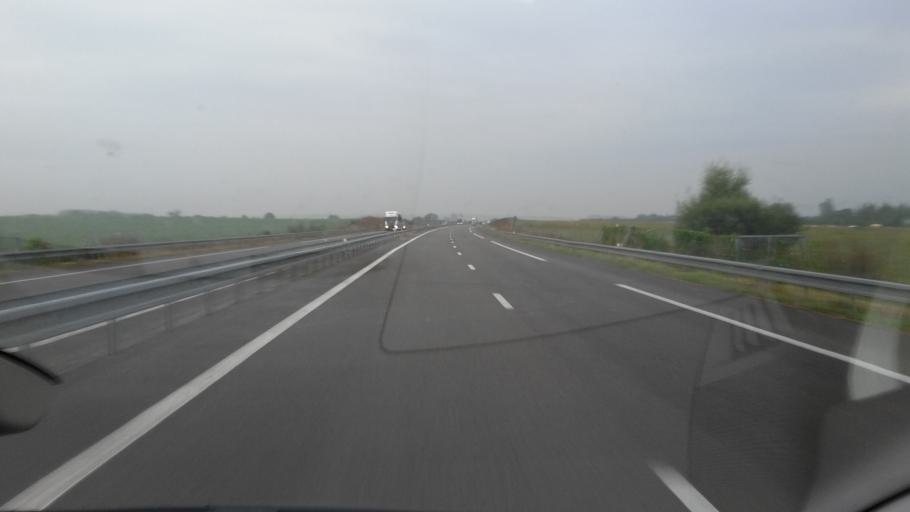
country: FR
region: Champagne-Ardenne
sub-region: Departement des Ardennes
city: Rethel
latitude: 49.5566
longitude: 4.4584
